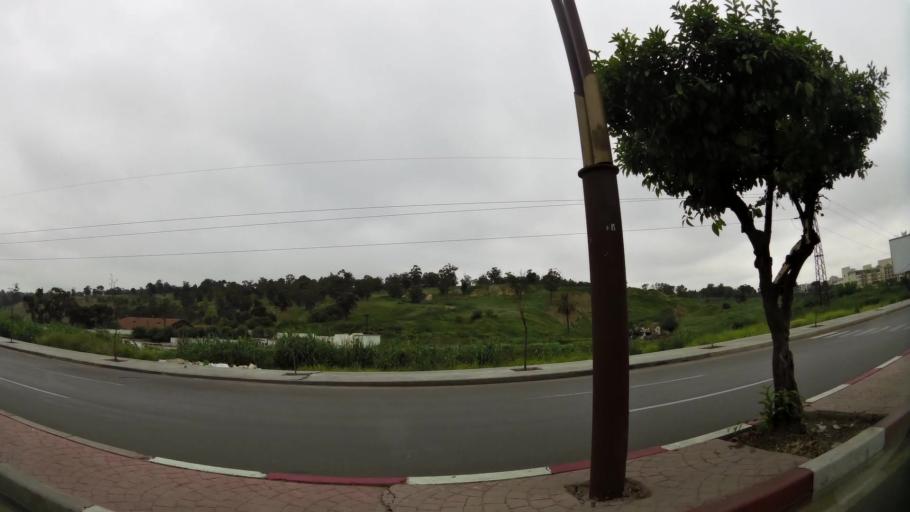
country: MA
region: Fes-Boulemane
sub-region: Fes
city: Fes
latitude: 34.0508
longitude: -4.9904
